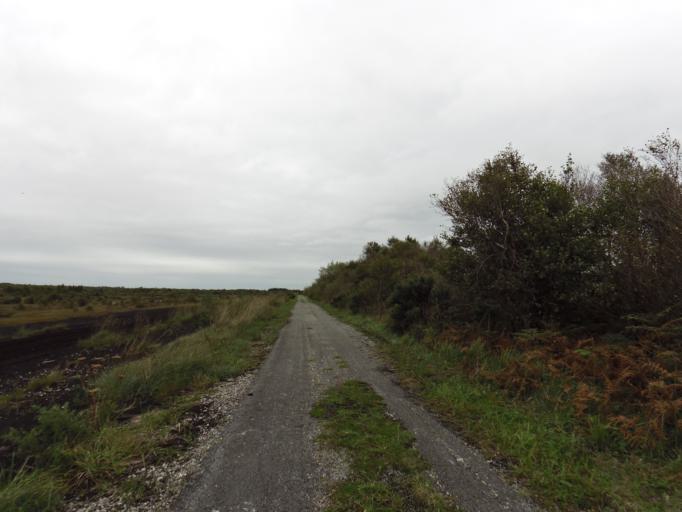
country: IE
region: Leinster
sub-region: Uibh Fhaili
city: Ferbane
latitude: 53.2509
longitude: -7.7514
